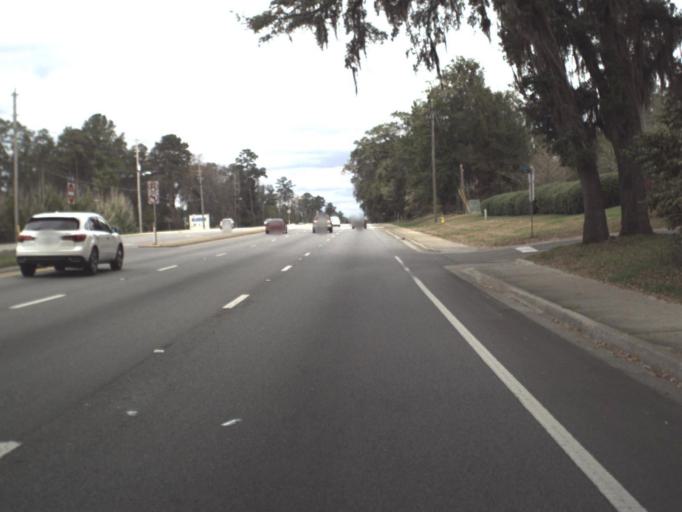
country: US
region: Florida
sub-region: Leon County
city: Tallahassee
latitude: 30.5440
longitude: -84.2271
